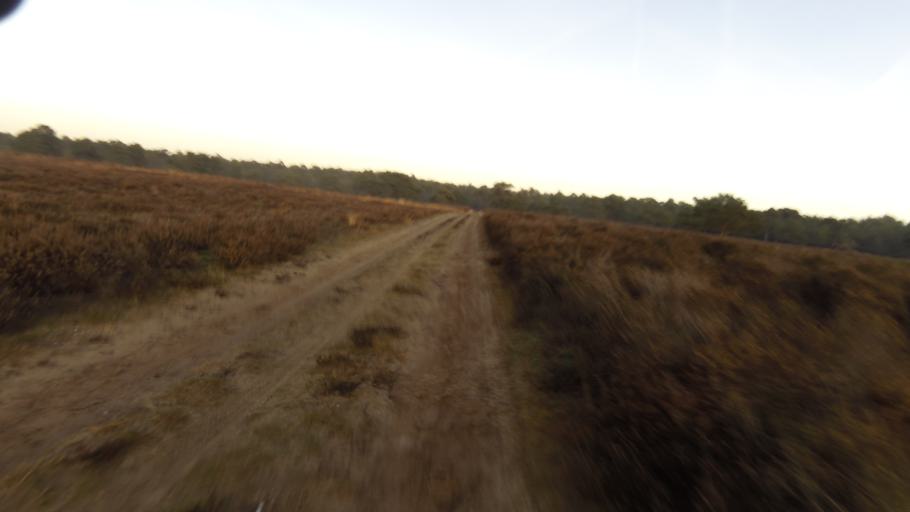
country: NL
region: Gelderland
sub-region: Gemeente Apeldoorn
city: Uddel
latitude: 52.2338
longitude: 5.8055
